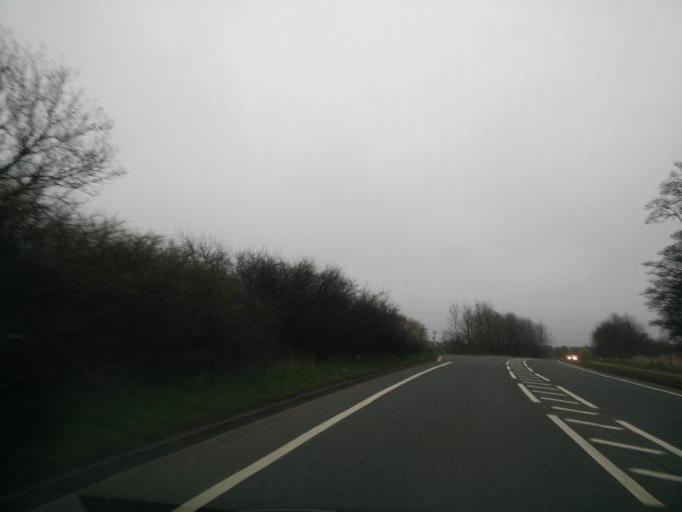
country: GB
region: England
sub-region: County Durham
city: Ushaw Moor
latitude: 54.7394
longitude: -1.6512
